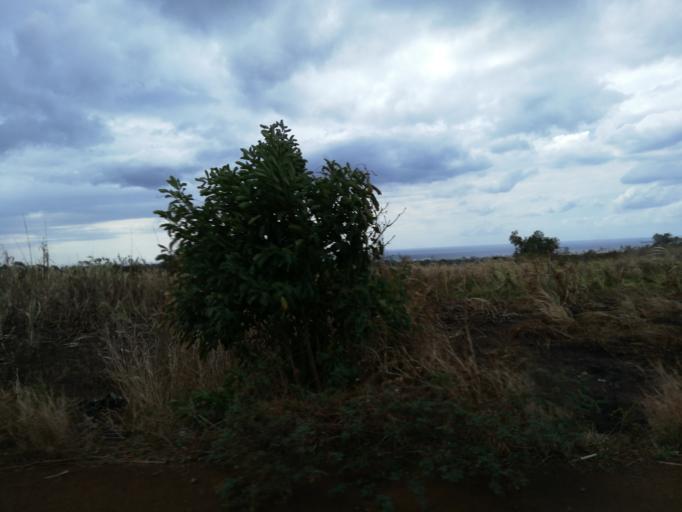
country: MU
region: Black River
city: Petite Riviere
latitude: -20.2076
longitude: 57.4568
